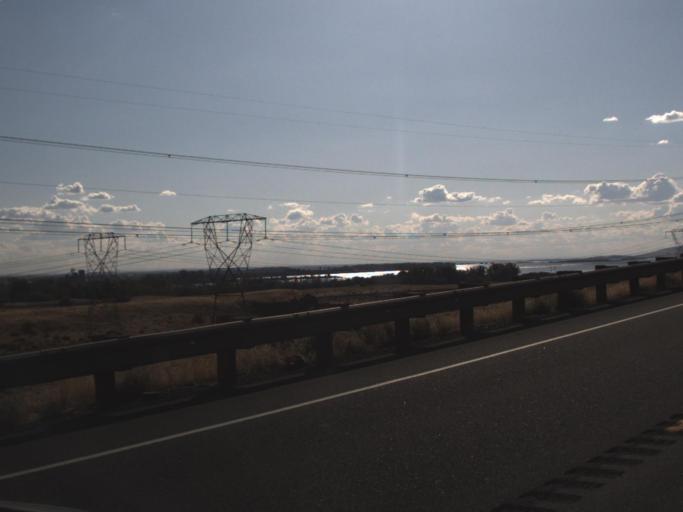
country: US
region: Oregon
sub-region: Morrow County
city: Irrigon
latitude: 45.9433
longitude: -119.5392
